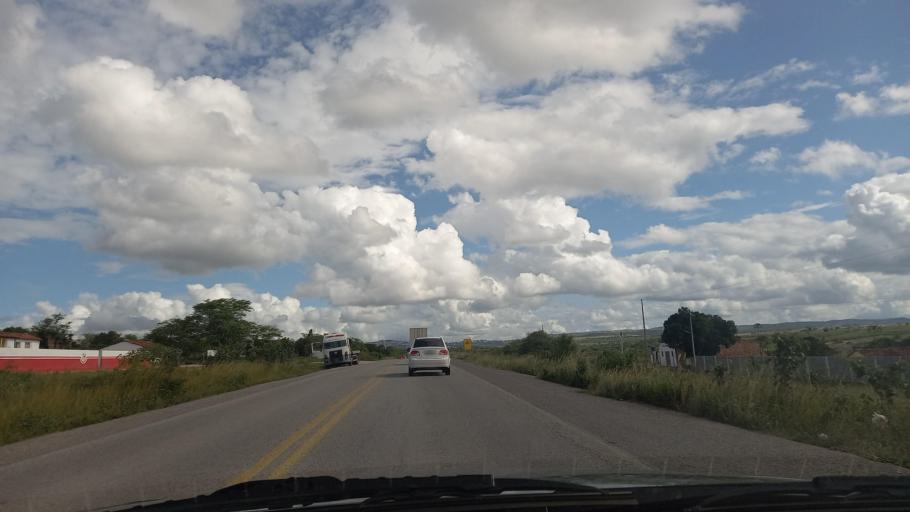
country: BR
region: Pernambuco
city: Garanhuns
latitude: -8.8102
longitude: -36.4436
